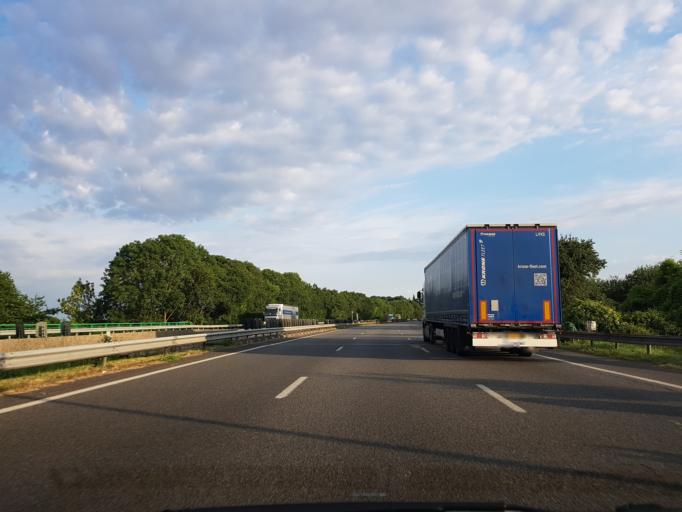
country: FR
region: Picardie
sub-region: Departement de l'Oise
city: Verberie
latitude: 49.2785
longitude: 2.6958
